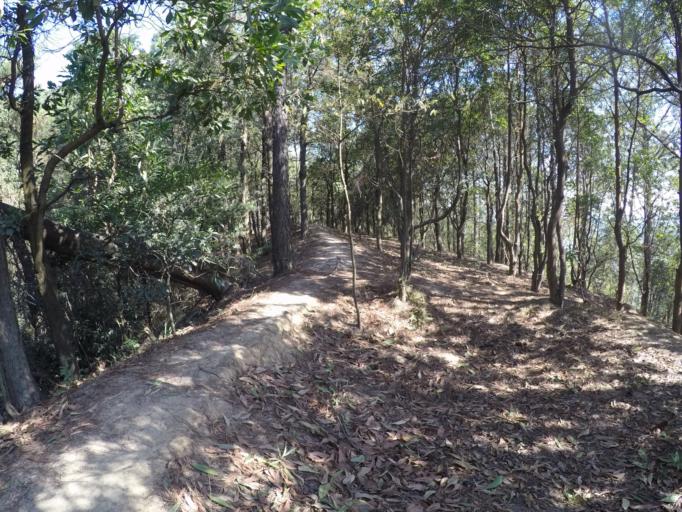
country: CN
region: Guangdong
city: Huancheng
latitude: 22.4695
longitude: 113.4150
